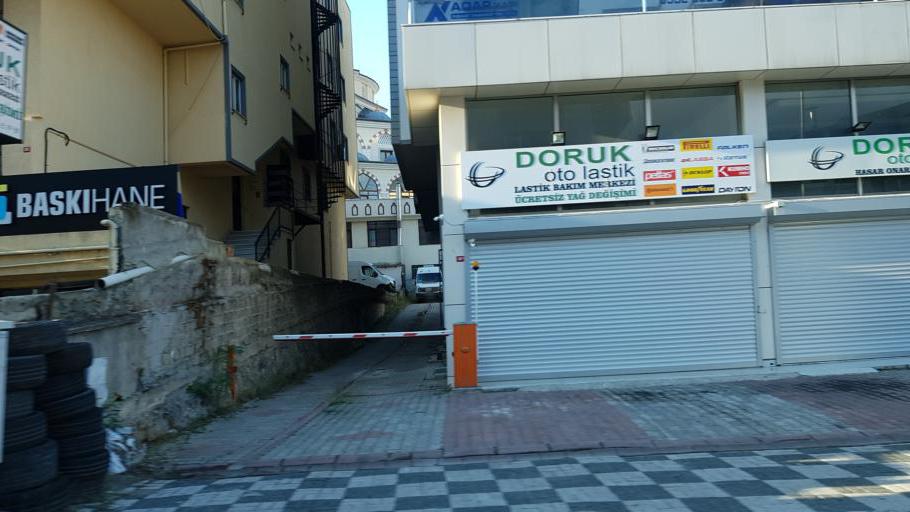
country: TR
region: Istanbul
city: Maltepe
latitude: 40.9423
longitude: 29.1482
